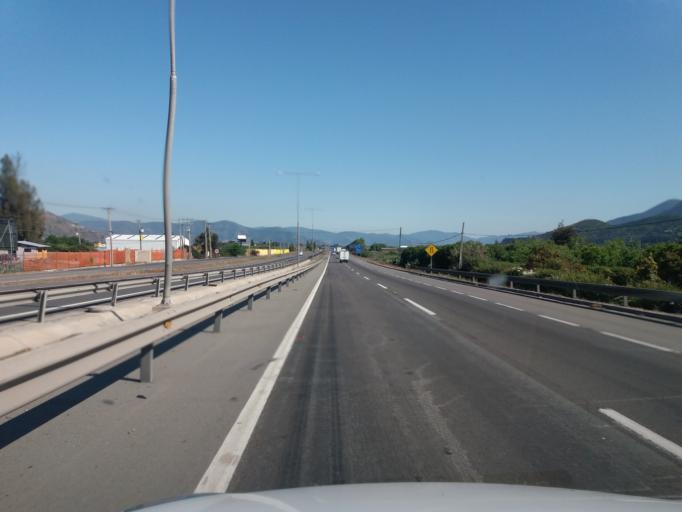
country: CL
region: Valparaiso
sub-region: Provincia de Quillota
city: Hacienda La Calera
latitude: -32.8137
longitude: -71.1449
